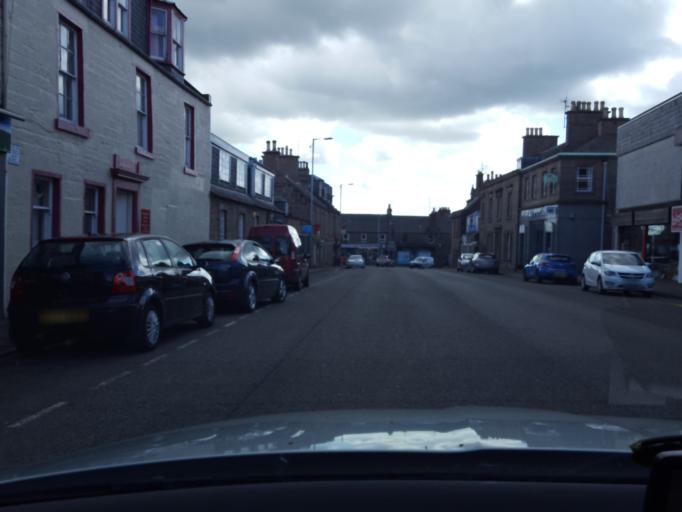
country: GB
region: Scotland
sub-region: Angus
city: Brechin
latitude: 56.7336
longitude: -2.6594
